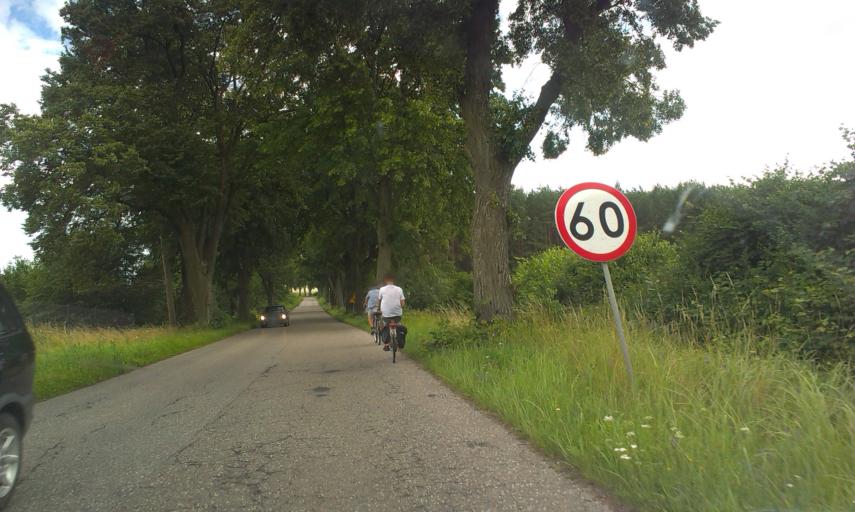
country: PL
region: Greater Poland Voivodeship
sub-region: Powiat zlotowski
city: Zlotow
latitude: 53.3940
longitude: 17.0007
